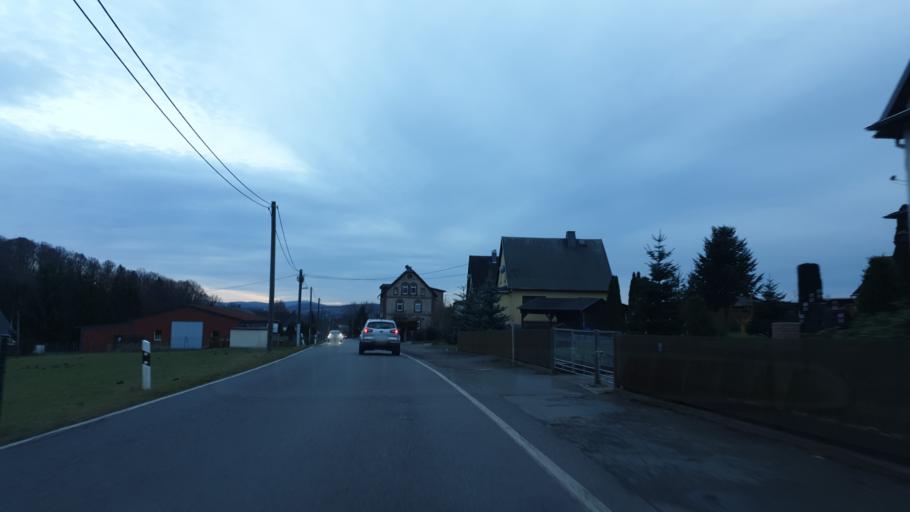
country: DE
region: Saxony
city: Hartenstein
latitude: 50.6830
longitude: 12.6690
